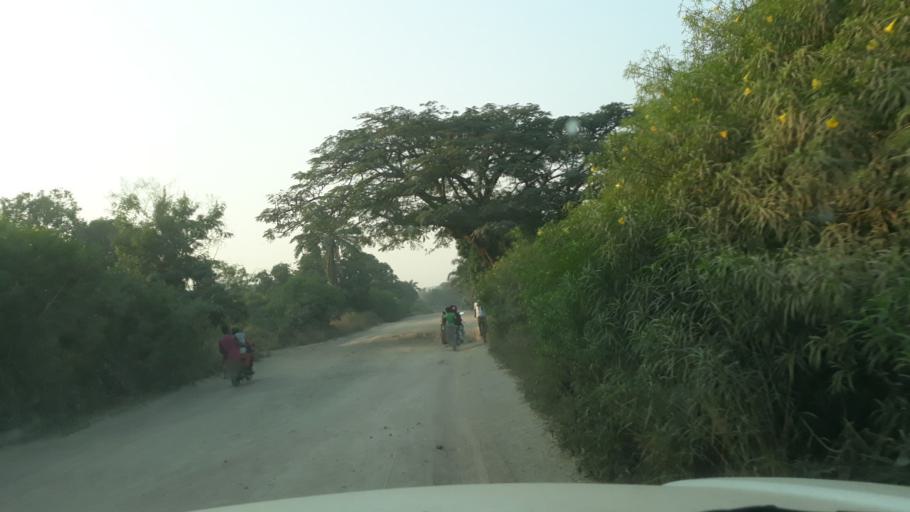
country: BI
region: Bururi
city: Rumonge
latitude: -4.1554
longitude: 29.0708
